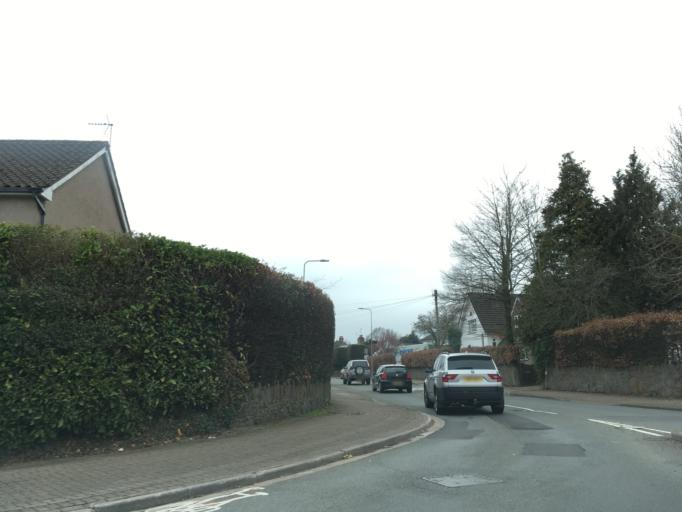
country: GB
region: Wales
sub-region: Cardiff
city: Cardiff
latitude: 51.5277
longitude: -3.1828
